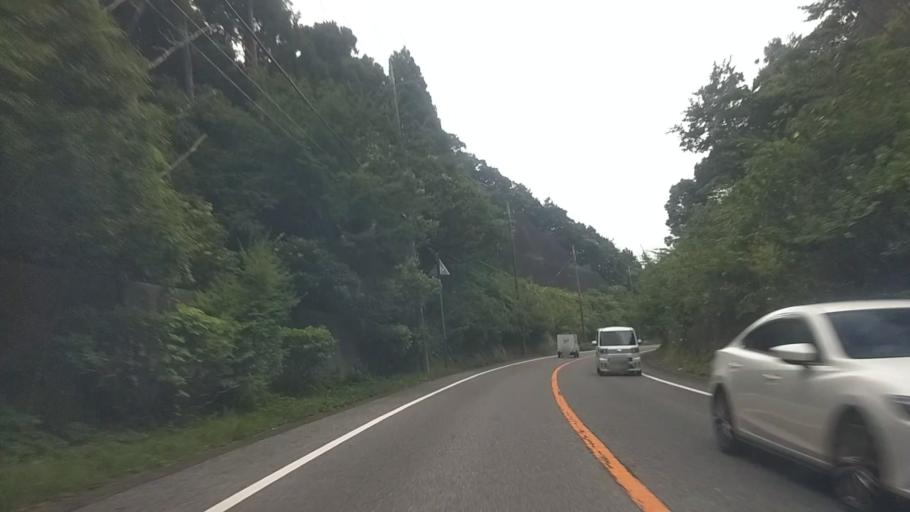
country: JP
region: Chiba
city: Kawaguchi
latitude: 35.1486
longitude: 140.0686
